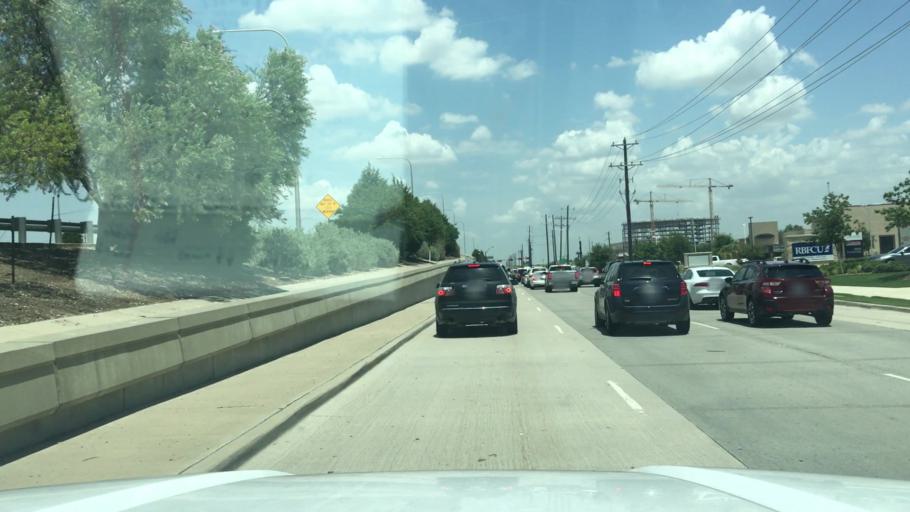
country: US
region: Texas
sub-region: Collin County
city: Frisco
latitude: 33.1724
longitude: -96.8393
